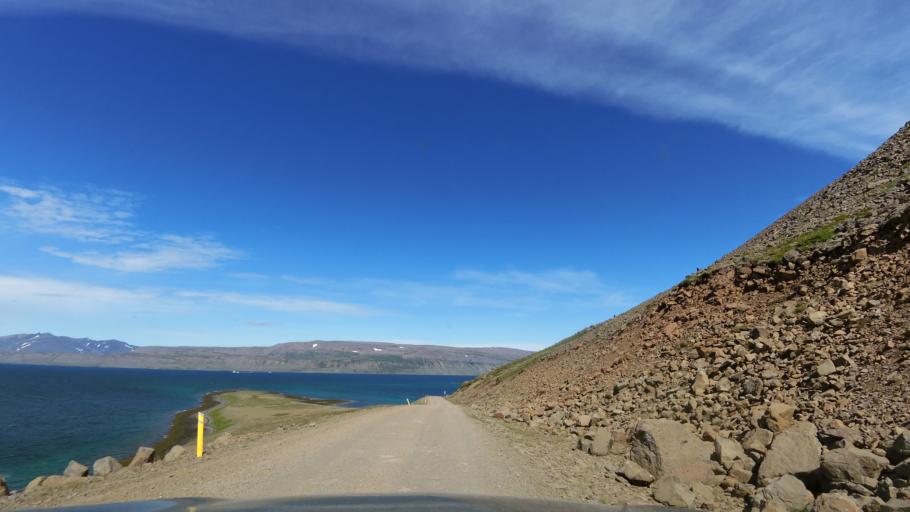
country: IS
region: Westfjords
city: Isafjoerdur
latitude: 65.6294
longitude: -23.5048
